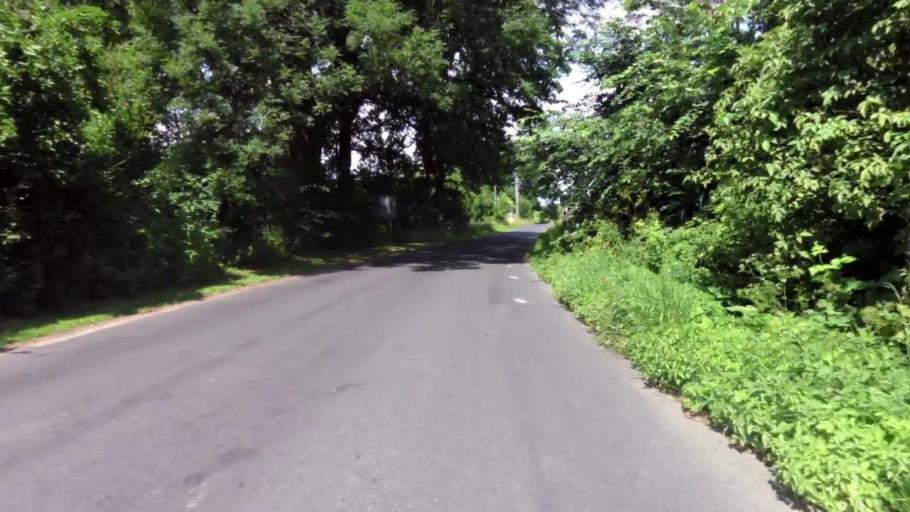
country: PL
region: West Pomeranian Voivodeship
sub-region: Powiat stargardzki
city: Dobrzany
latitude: 53.4248
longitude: 15.4683
